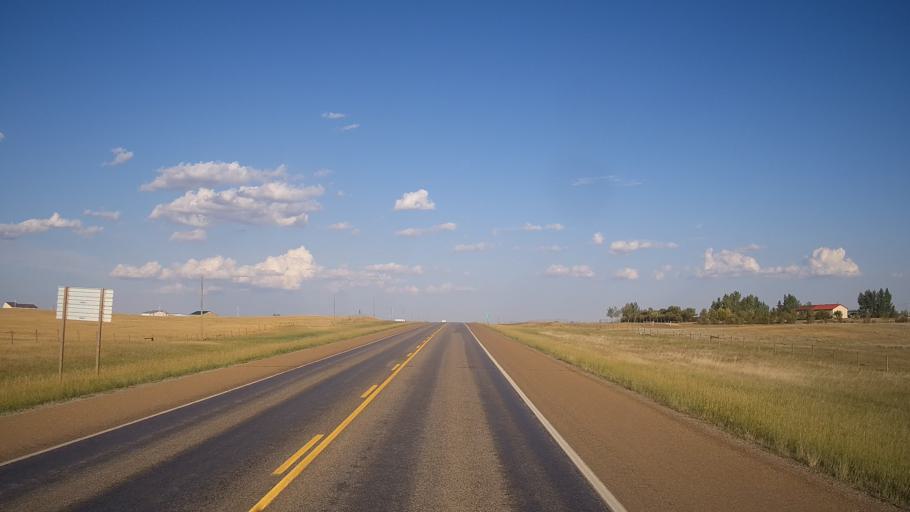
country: CA
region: Alberta
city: Hanna
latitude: 51.6297
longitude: -111.9135
